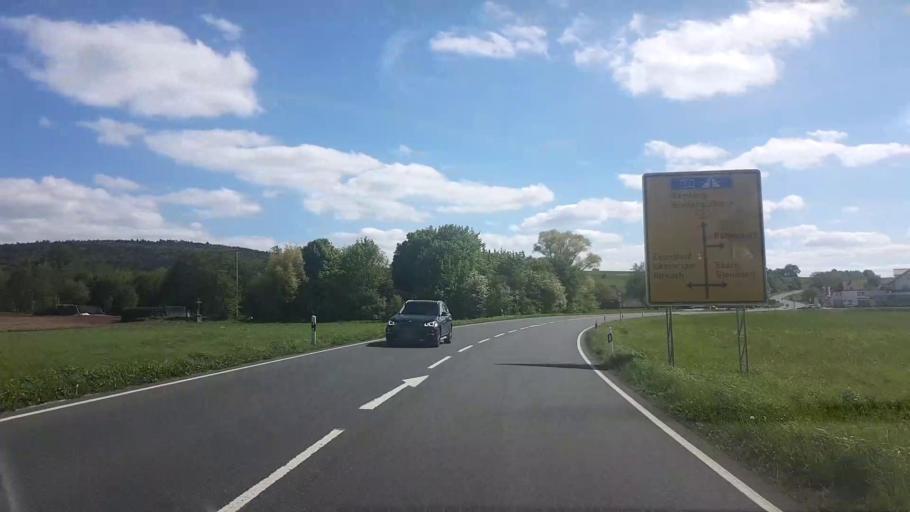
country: DE
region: Bavaria
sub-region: Regierungsbezirk Unterfranken
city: Untermerzbach
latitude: 50.0825
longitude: 10.8674
